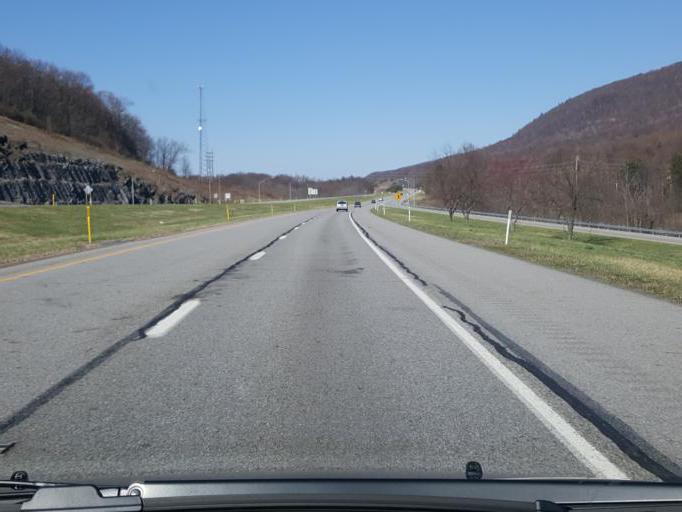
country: US
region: Pennsylvania
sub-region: Bedford County
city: Bedford
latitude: 40.1472
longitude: -78.5095
